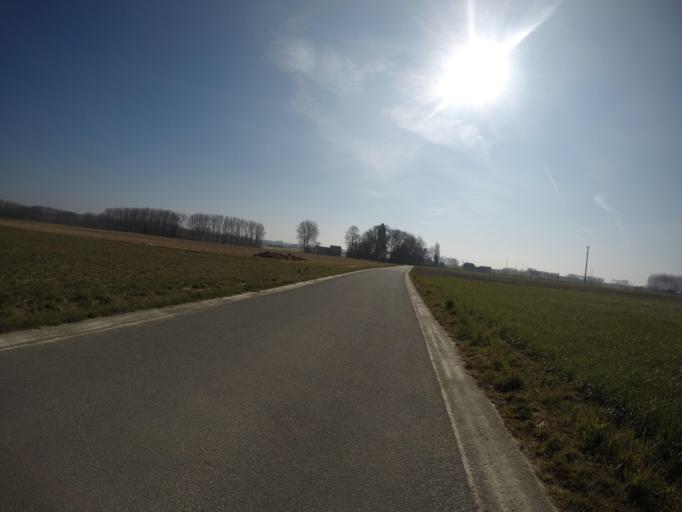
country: BE
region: Flanders
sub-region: Provincie Oost-Vlaanderen
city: Geraardsbergen
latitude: 50.7861
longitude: 3.8528
